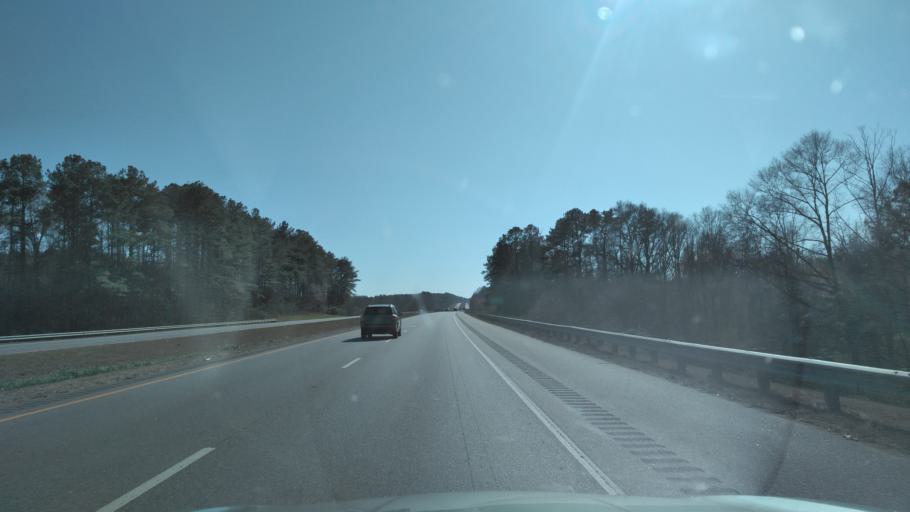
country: US
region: Alabama
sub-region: Butler County
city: Greenville
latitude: 31.8769
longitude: -86.6146
